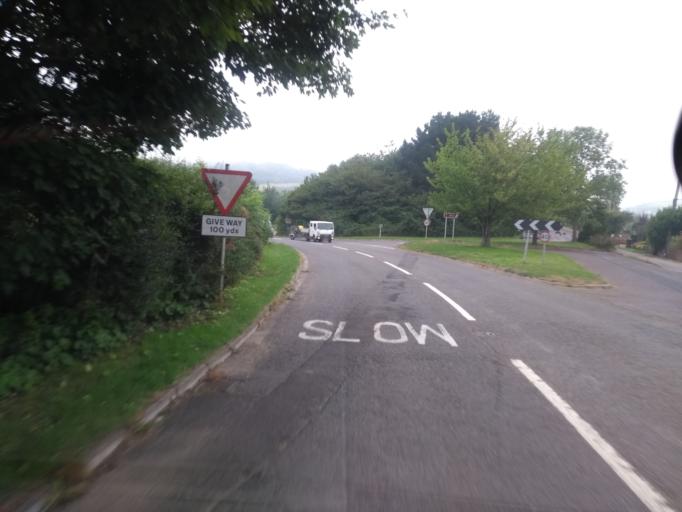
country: GB
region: England
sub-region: Dorset
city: Bridport
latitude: 50.7345
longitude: -2.7835
